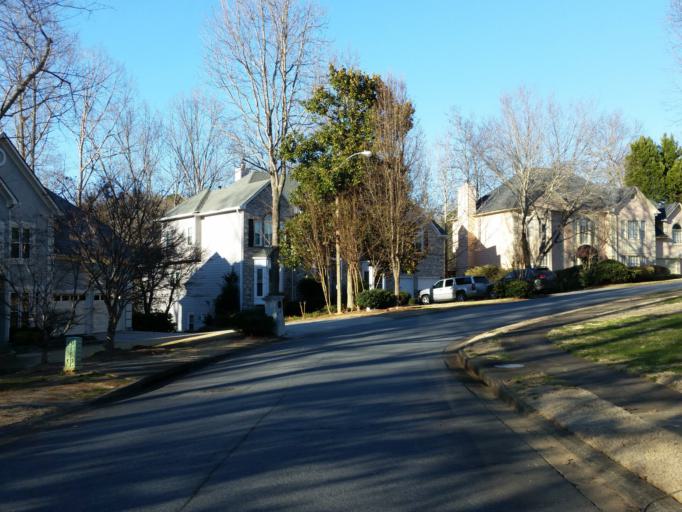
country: US
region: Georgia
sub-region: Cherokee County
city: Woodstock
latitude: 34.0569
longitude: -84.4772
